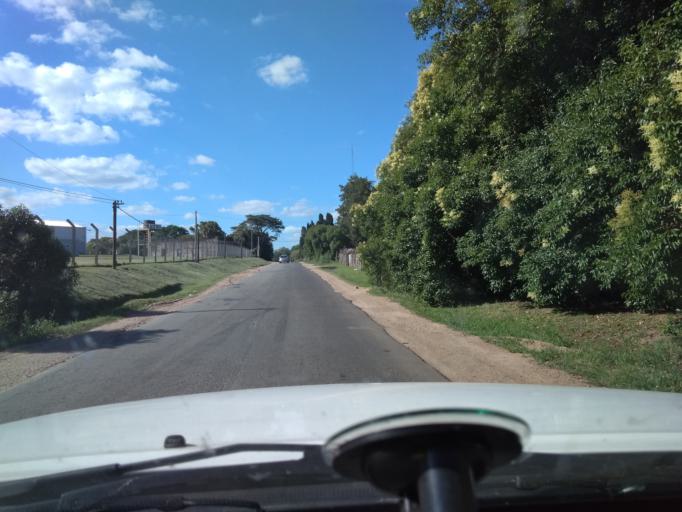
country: UY
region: Canelones
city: La Paz
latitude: -34.8036
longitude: -56.2099
